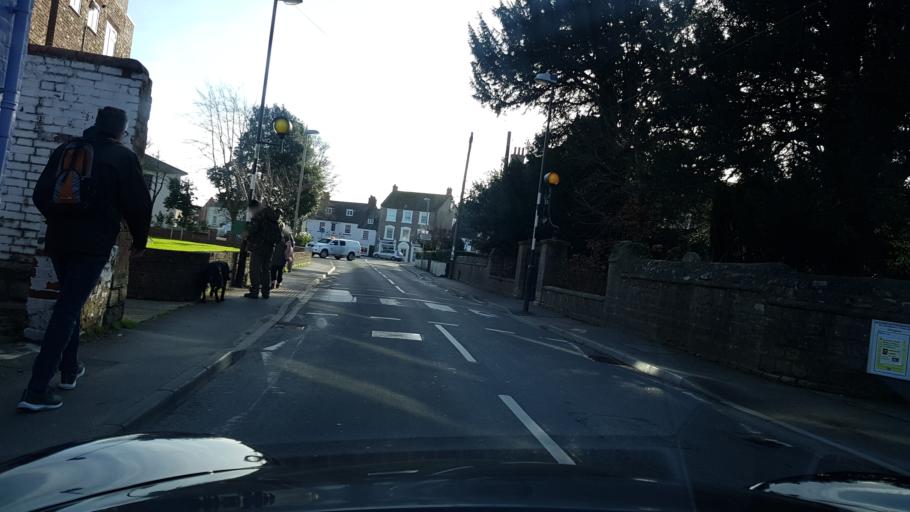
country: GB
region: England
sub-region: Dorset
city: Bridport
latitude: 50.7352
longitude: -2.7639
